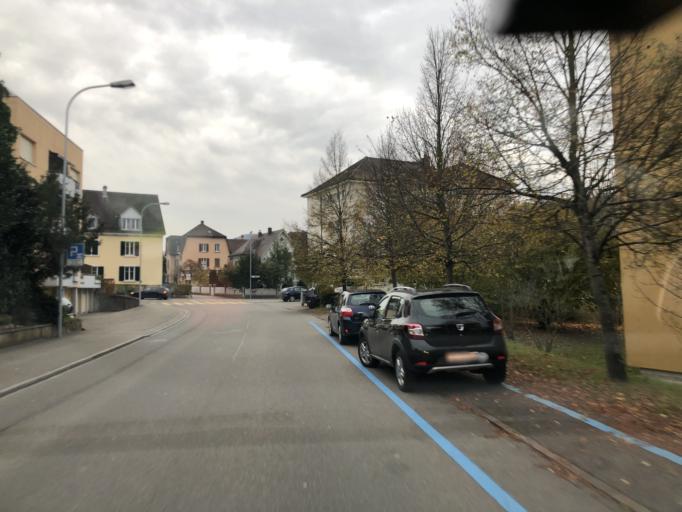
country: CH
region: Aargau
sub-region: Bezirk Baden
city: Neuenhof
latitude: 47.4598
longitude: 8.3188
